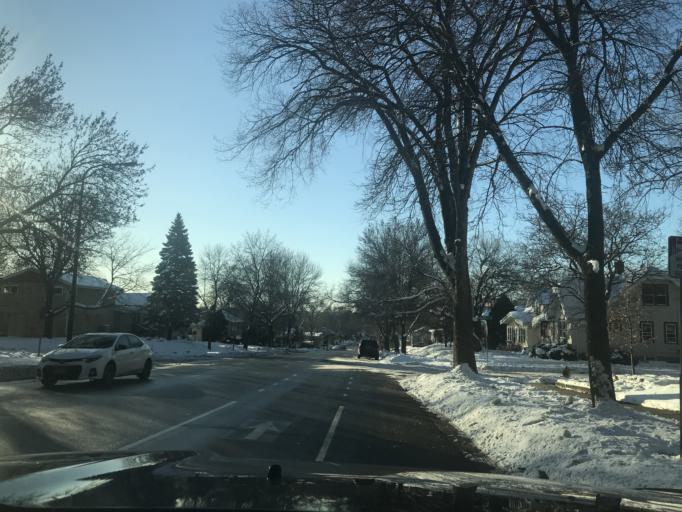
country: US
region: Minnesota
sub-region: Dakota County
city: Mendota Heights
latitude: 44.9290
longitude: -93.1467
